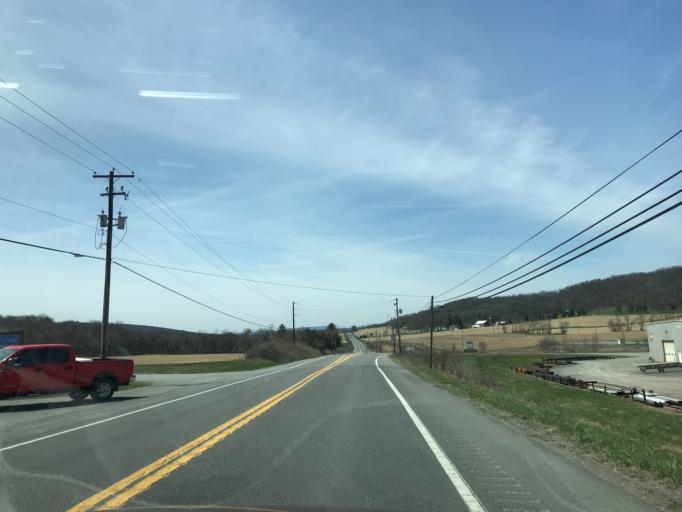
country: US
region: Pennsylvania
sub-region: Snyder County
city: Selinsgrove
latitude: 40.8060
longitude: -76.9171
